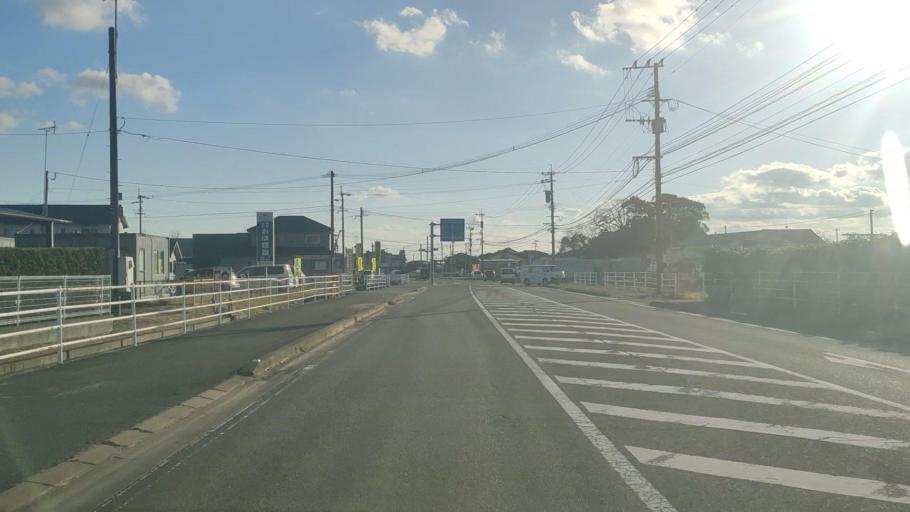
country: JP
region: Saga Prefecture
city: Saga-shi
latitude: 33.3108
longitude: 130.2647
